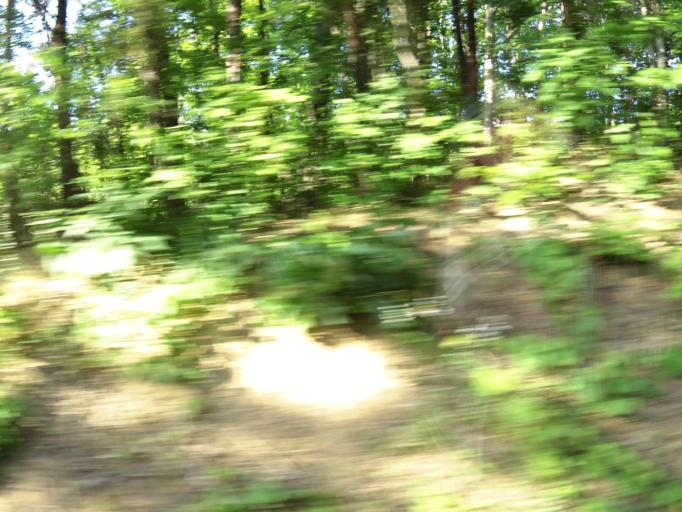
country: US
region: Tennessee
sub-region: Sevier County
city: Sevierville
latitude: 35.8264
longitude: -83.6016
